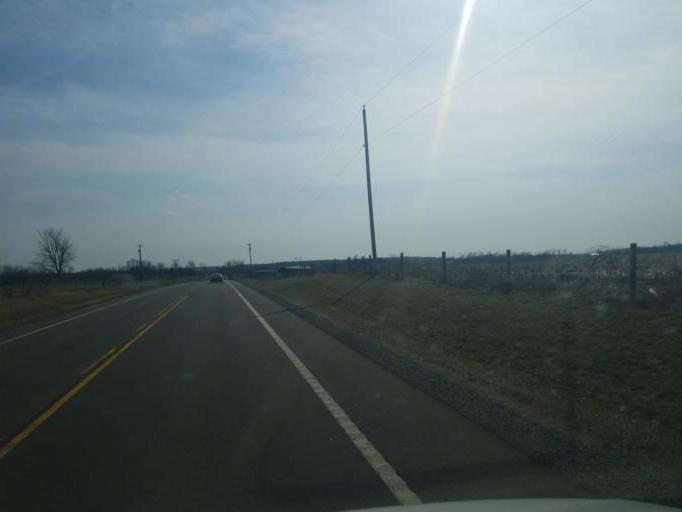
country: US
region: Ohio
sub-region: Logan County
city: Northwood
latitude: 40.4601
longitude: -83.7203
